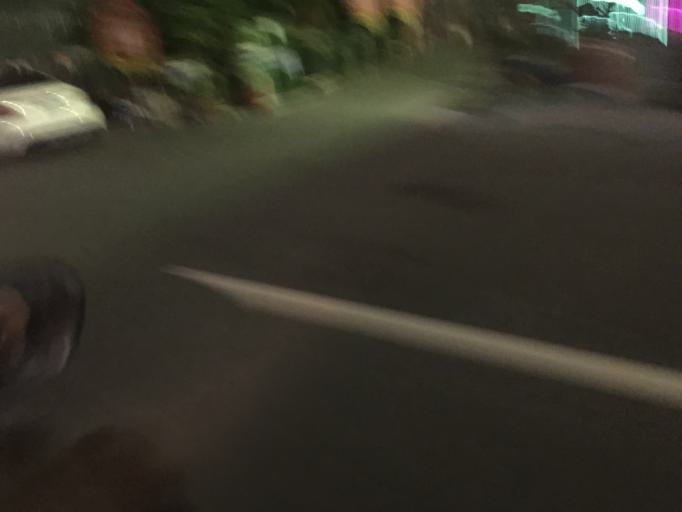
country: TW
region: Taiwan
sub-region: Hsinchu
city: Hsinchu
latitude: 24.8084
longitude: 120.9588
